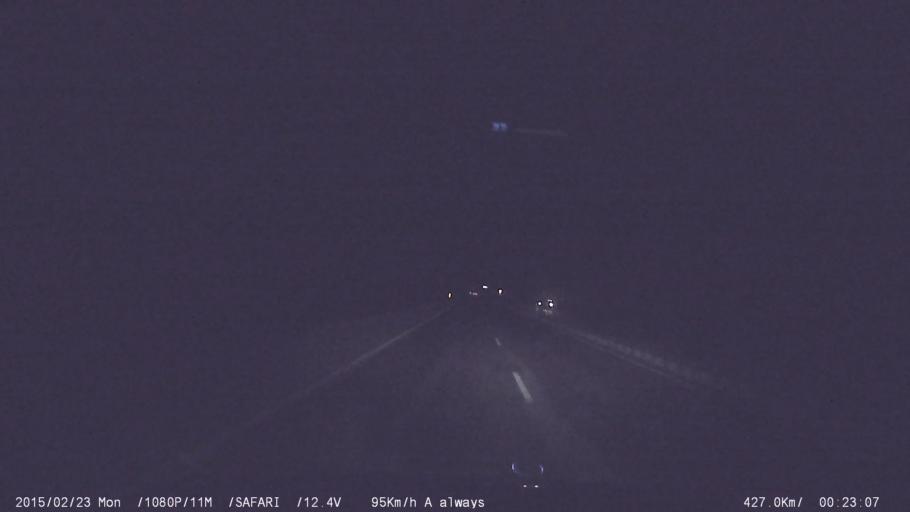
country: IN
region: Tamil Nadu
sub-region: Salem
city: Omalur
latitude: 11.9197
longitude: 78.0620
